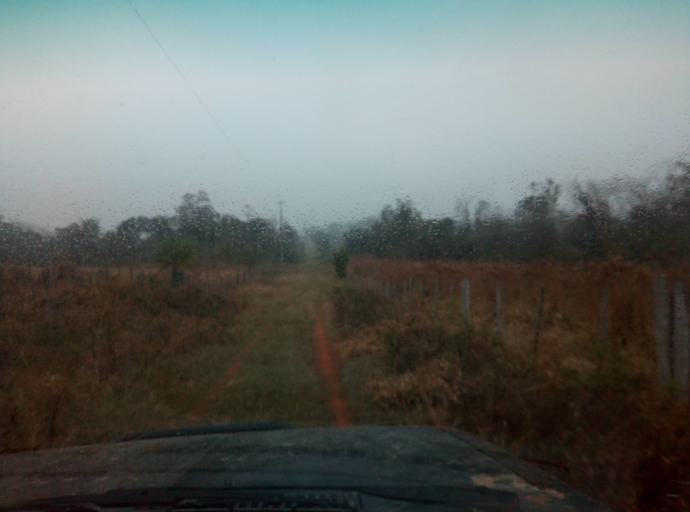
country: PY
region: Caaguazu
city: Doctor Cecilio Baez
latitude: -25.1543
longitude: -56.2611
